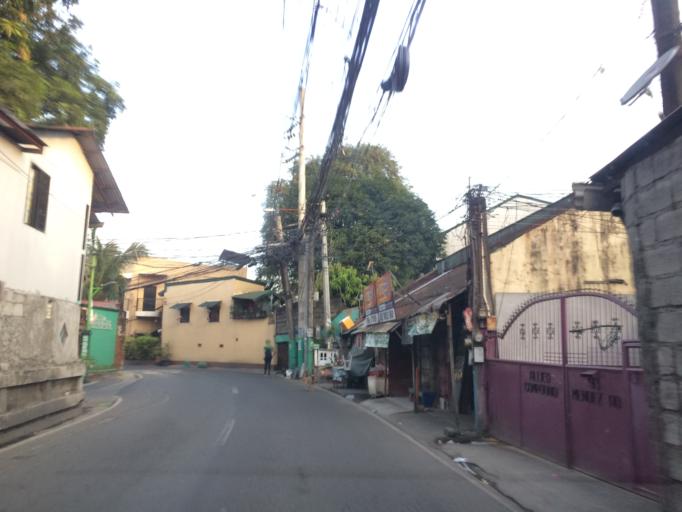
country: PH
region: Calabarzon
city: Bagong Pagasa
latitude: 14.6692
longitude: 121.0152
